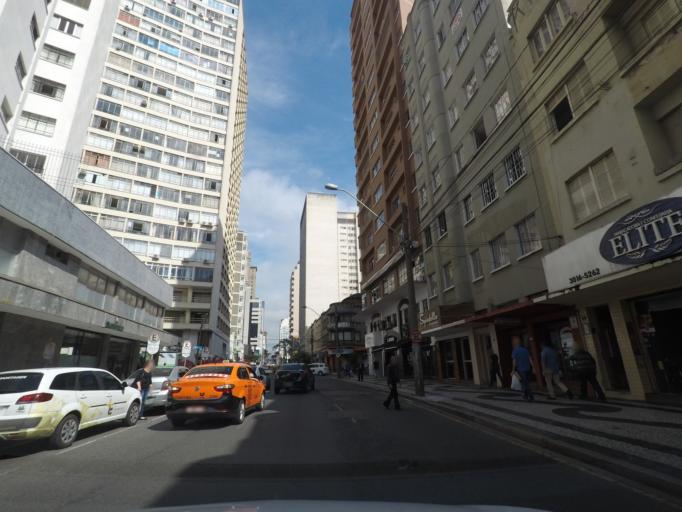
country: BR
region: Parana
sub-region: Curitiba
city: Curitiba
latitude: -25.4314
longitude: -49.2757
